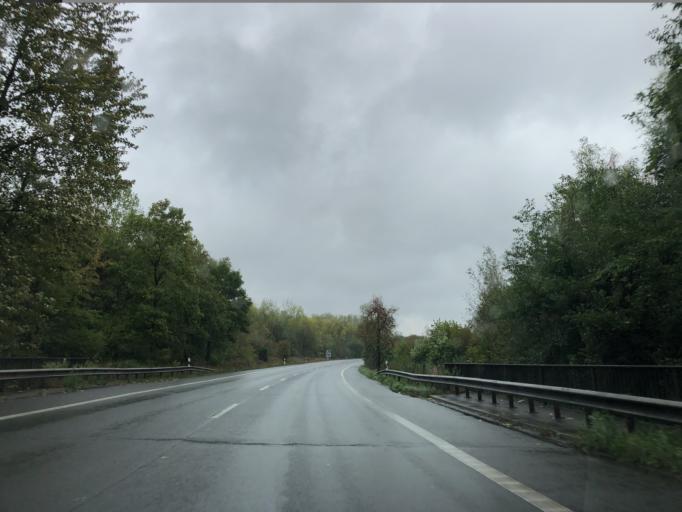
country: DE
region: North Rhine-Westphalia
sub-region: Regierungsbezirk Koln
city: Bedburg
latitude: 51.0239
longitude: 6.5817
